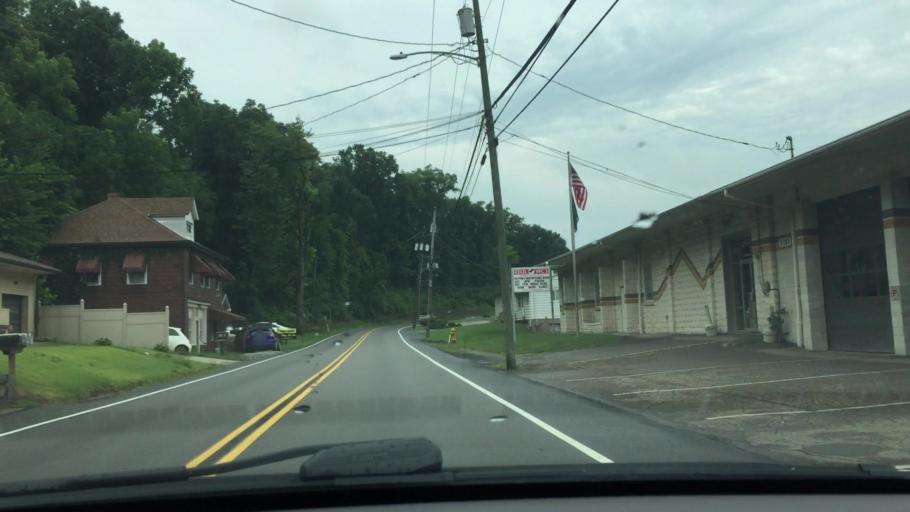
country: US
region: Pennsylvania
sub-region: Washington County
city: Cecil-Bishop
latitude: 40.3222
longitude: -80.1989
